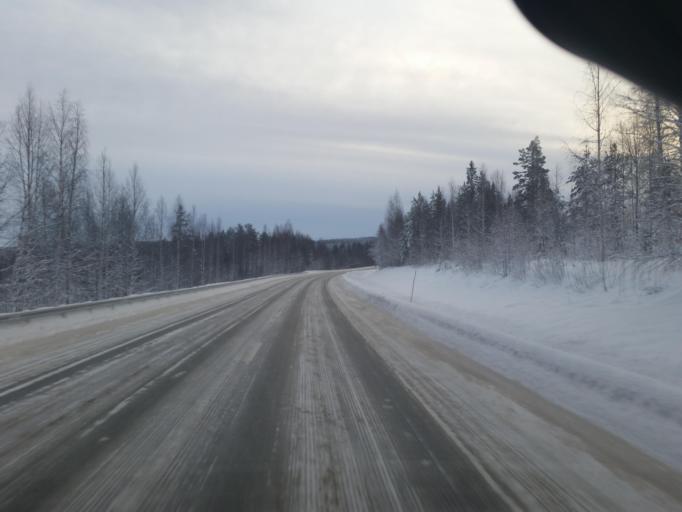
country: SE
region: Norrbotten
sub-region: Pitea Kommun
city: Norrfjarden
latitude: 65.6306
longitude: 21.3899
